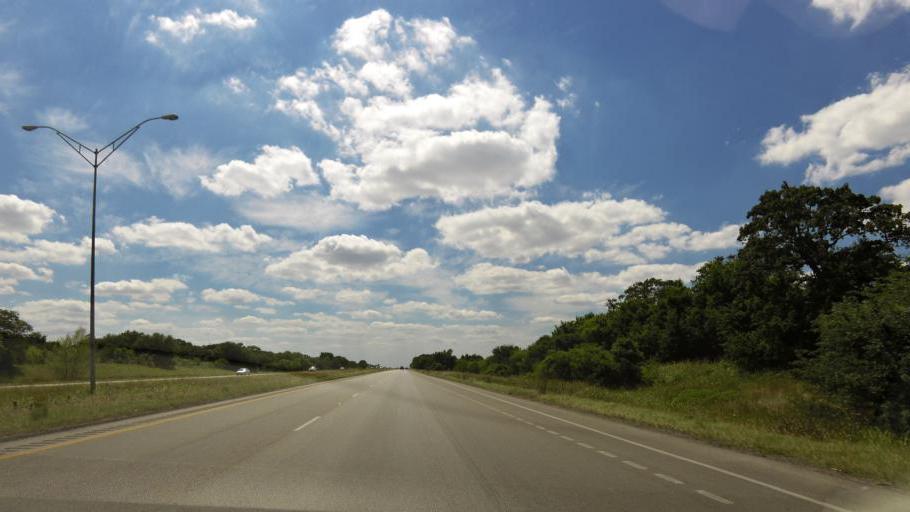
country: US
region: Texas
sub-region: Fayette County
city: Flatonia
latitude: 29.6967
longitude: -97.1128
